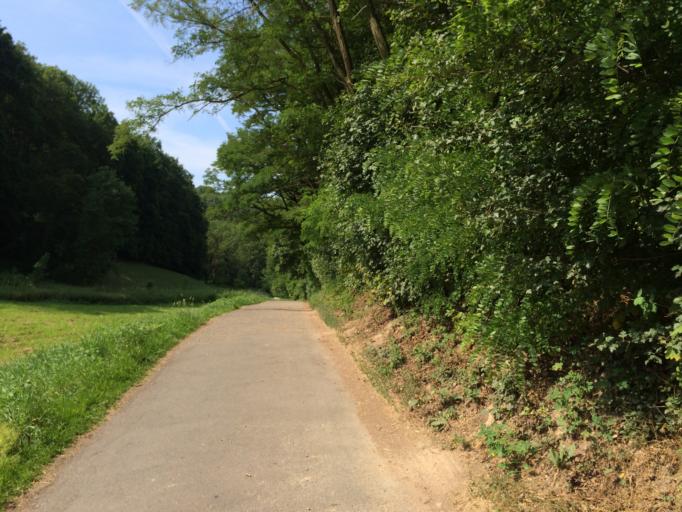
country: CZ
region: Central Bohemia
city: Horomerice
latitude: 50.0984
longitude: 14.3175
